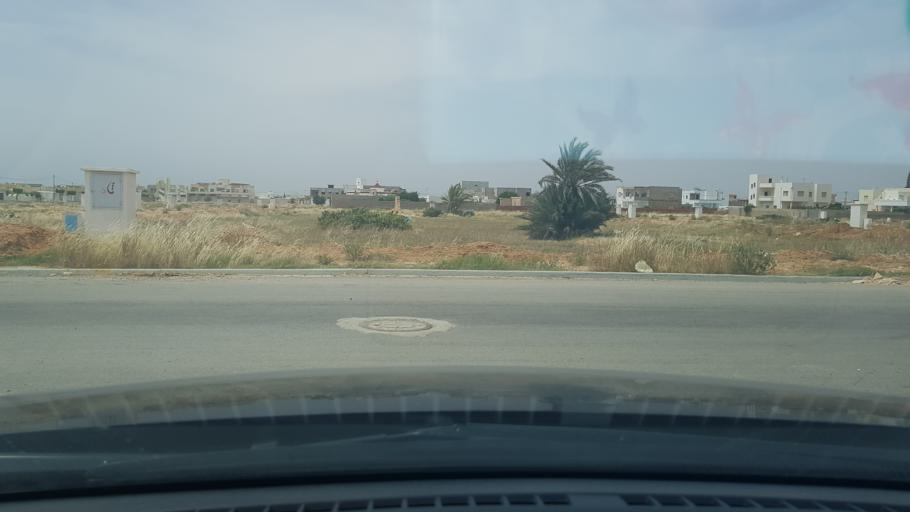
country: TN
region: Safaqis
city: Al Qarmadah
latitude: 34.8235
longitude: 10.7435
